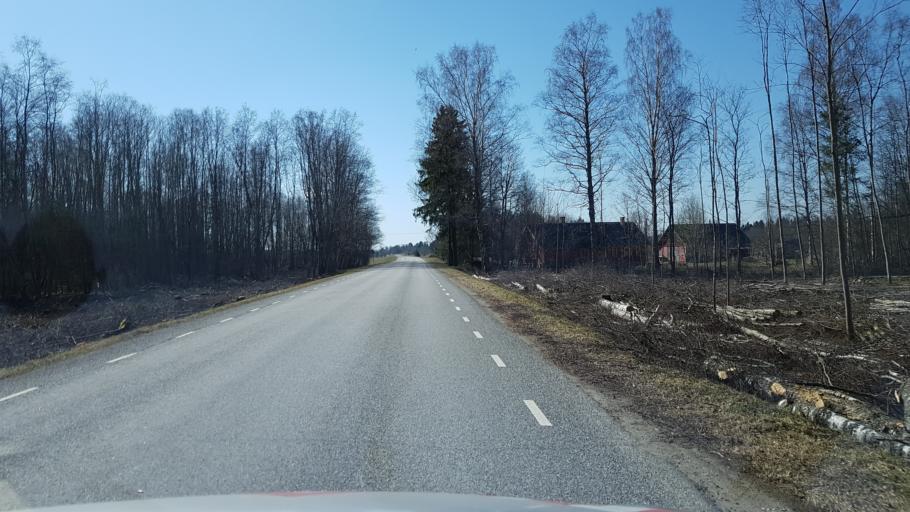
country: EE
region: Ida-Virumaa
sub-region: Kohtla-Nomme vald
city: Kohtla-Nomme
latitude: 59.2988
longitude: 27.2376
